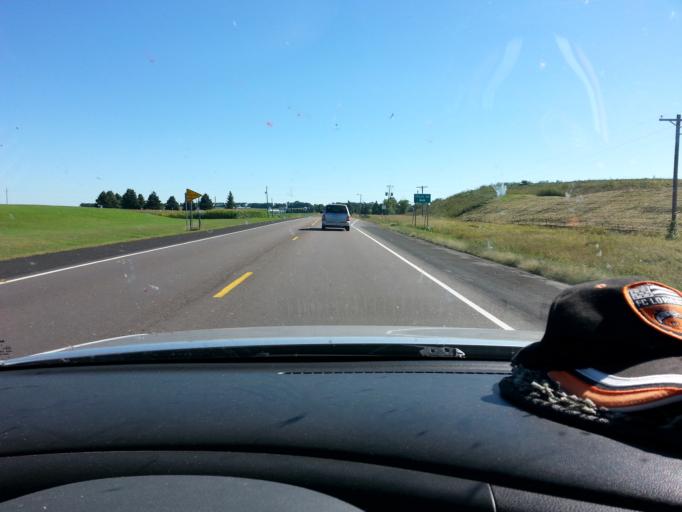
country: US
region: Minnesota
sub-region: Dakota County
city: Rosemount
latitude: 44.7050
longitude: -93.1366
